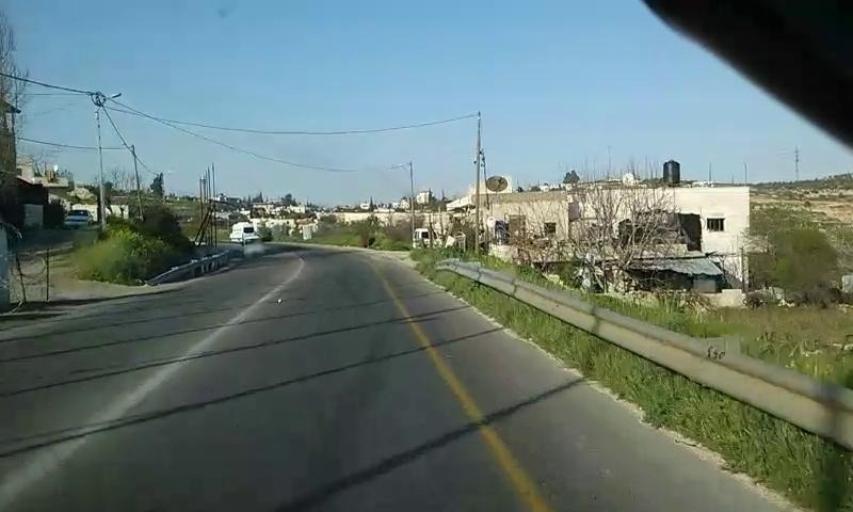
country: PS
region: West Bank
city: Bayt Ummar
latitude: 31.6152
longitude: 35.1145
